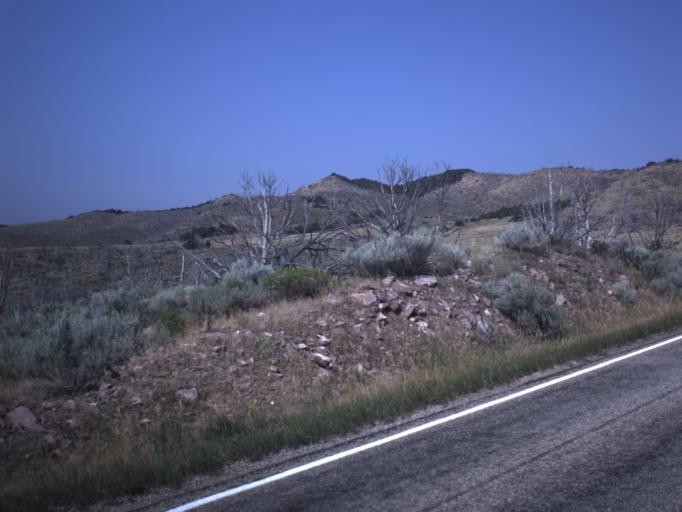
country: US
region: Utah
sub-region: Daggett County
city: Manila
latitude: 40.9462
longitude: -109.4378
